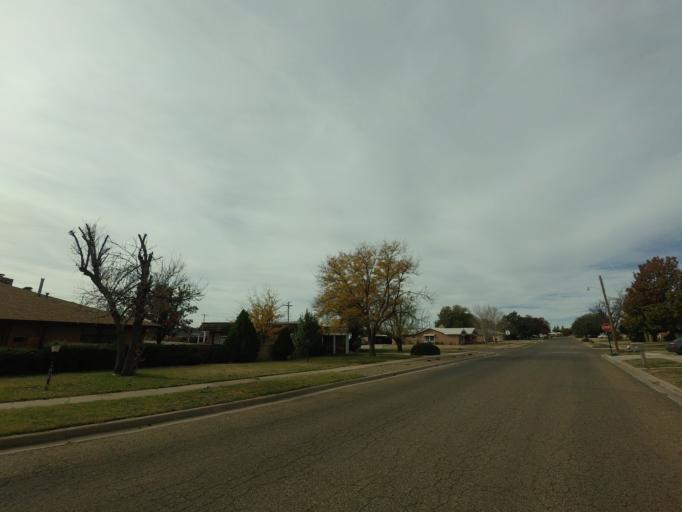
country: US
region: New Mexico
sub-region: Curry County
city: Clovis
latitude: 34.4213
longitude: -103.2111
